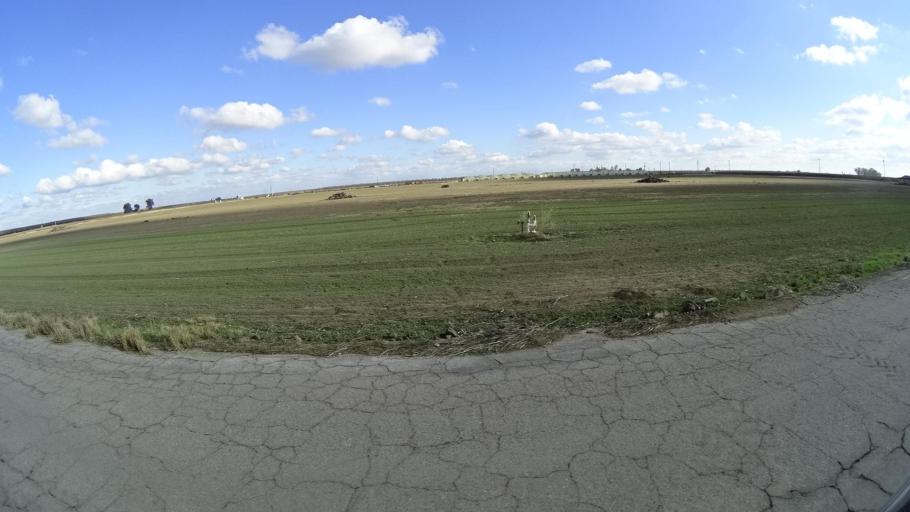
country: US
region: California
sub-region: Kern County
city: Delano
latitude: 35.7418
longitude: -119.3478
